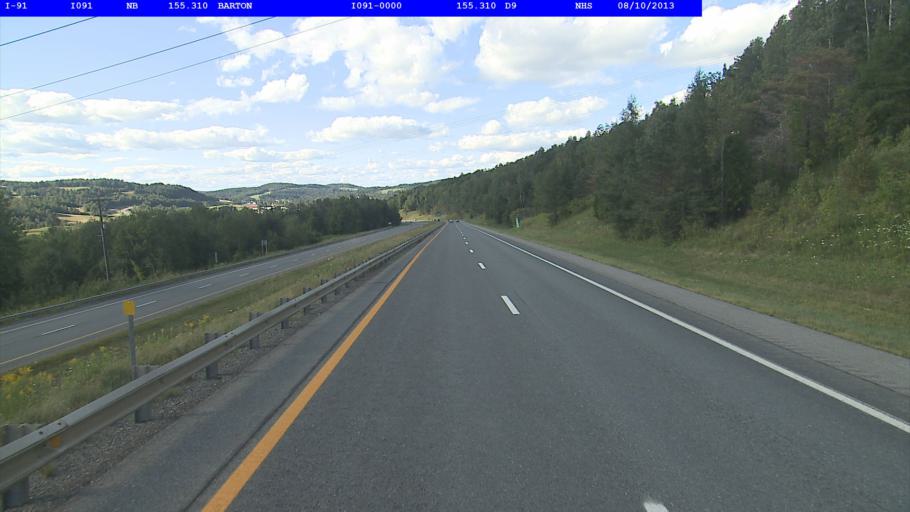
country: US
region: Vermont
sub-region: Orleans County
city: Newport
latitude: 44.7271
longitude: -72.1801
